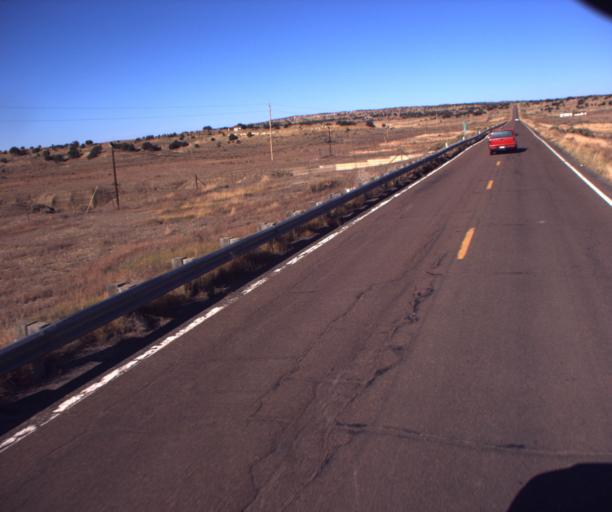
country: US
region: Arizona
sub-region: Apache County
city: Ganado
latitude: 35.7487
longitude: -109.8749
